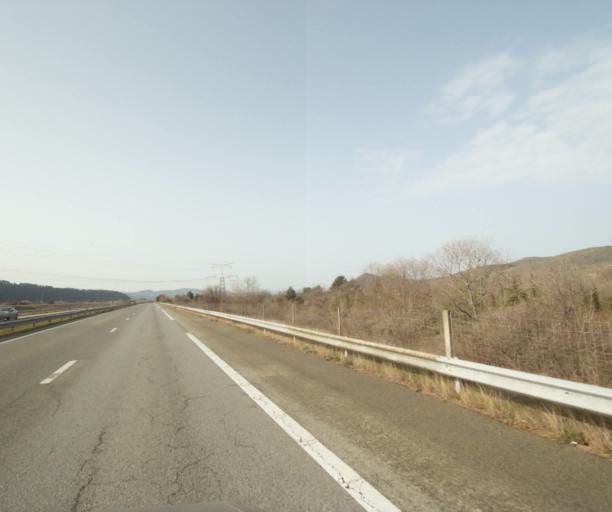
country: FR
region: Provence-Alpes-Cote d'Azur
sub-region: Departement des Bouches-du-Rhone
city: Jouques
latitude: 43.6670
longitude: 5.6361
